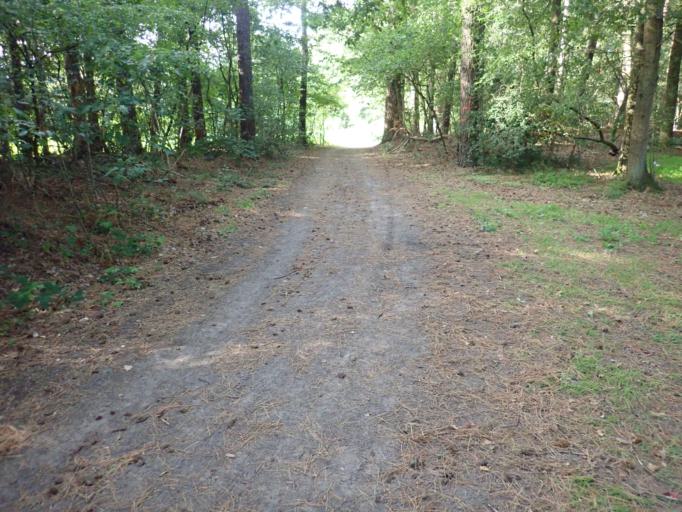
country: BE
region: Flanders
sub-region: Provincie Antwerpen
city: Lille
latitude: 51.2821
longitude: 4.8014
